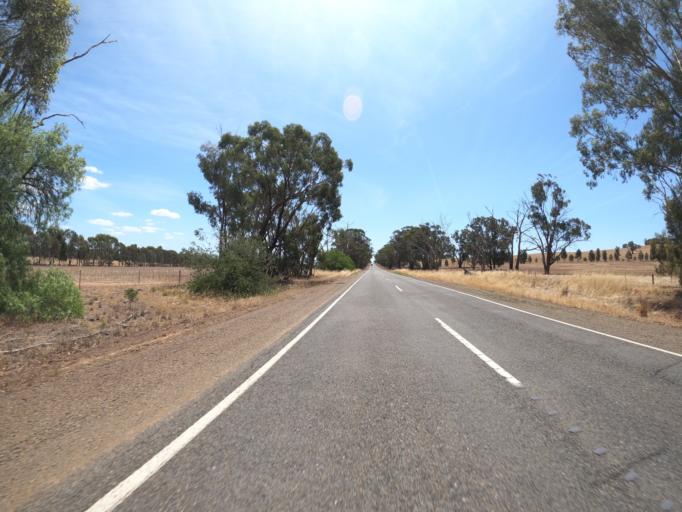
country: AU
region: Victoria
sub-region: Benalla
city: Benalla
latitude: -36.3549
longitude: 145.9648
